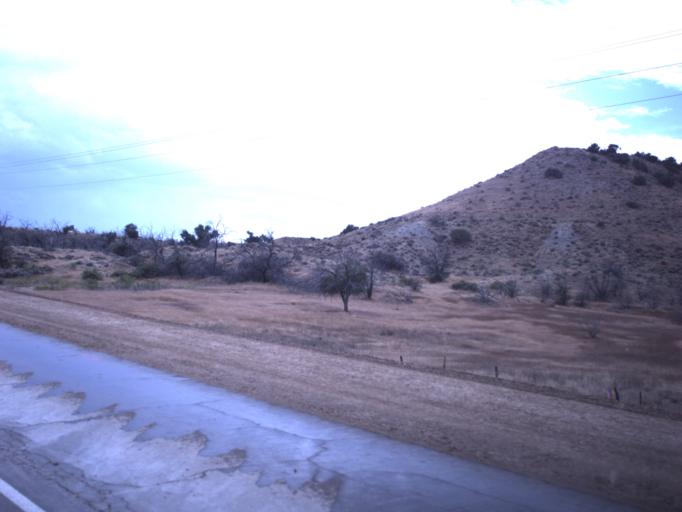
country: US
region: Utah
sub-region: Duchesne County
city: Roosevelt
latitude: 40.2511
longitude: -110.0674
